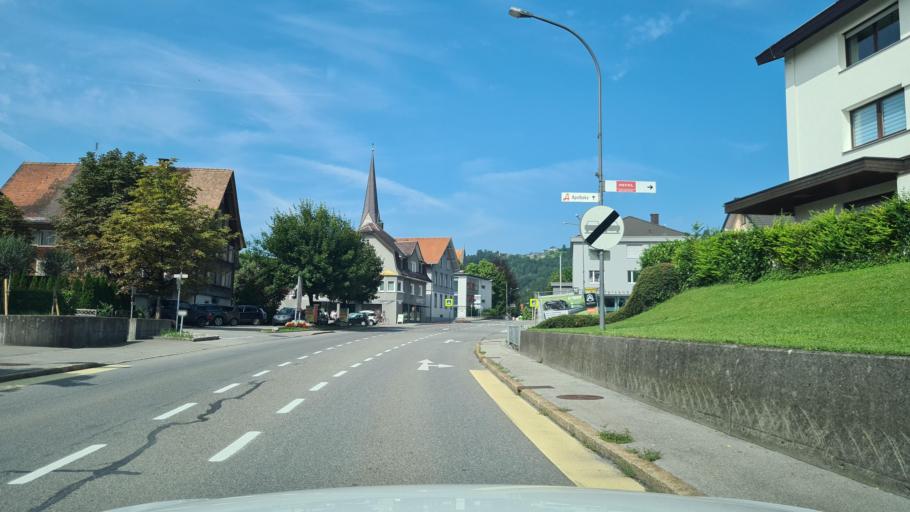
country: AT
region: Vorarlberg
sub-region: Politischer Bezirk Bregenz
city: Schwarzach
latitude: 47.4432
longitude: 9.7623
